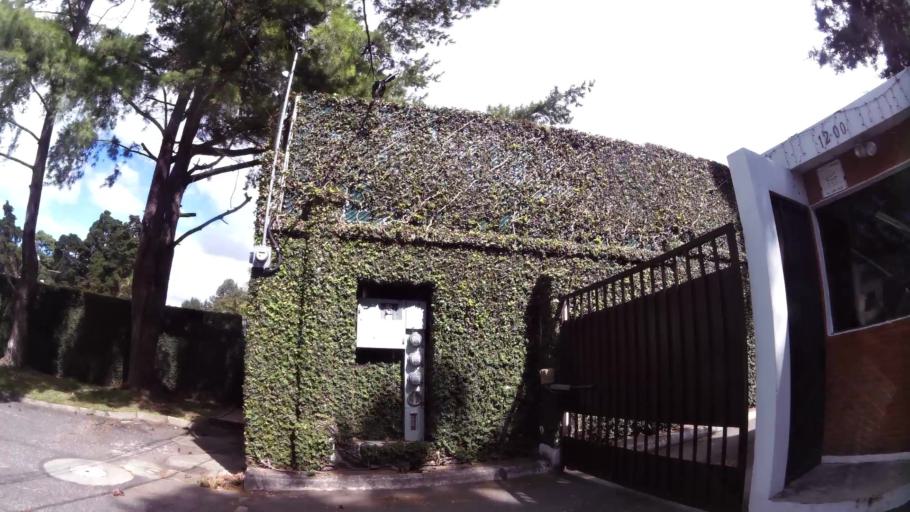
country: GT
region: Guatemala
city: Santa Catarina Pinula
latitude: 14.5826
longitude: -90.5119
